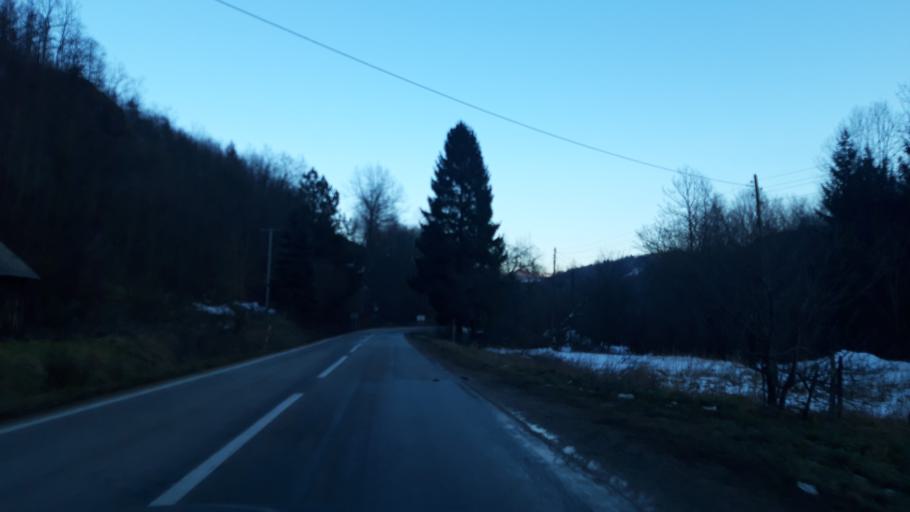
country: BA
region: Republika Srpska
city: Milici
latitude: 44.1656
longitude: 19.0391
